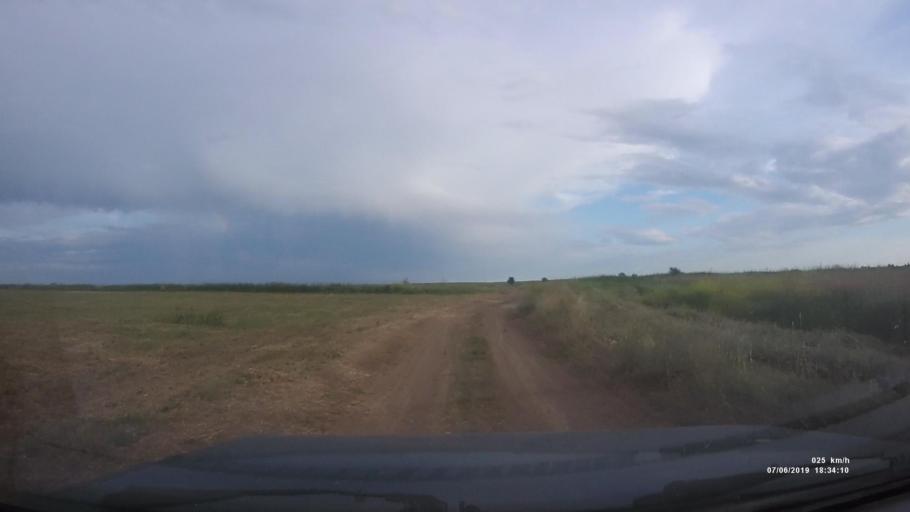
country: RU
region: Rostov
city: Staraya Stanitsa
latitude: 48.2590
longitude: 40.3622
